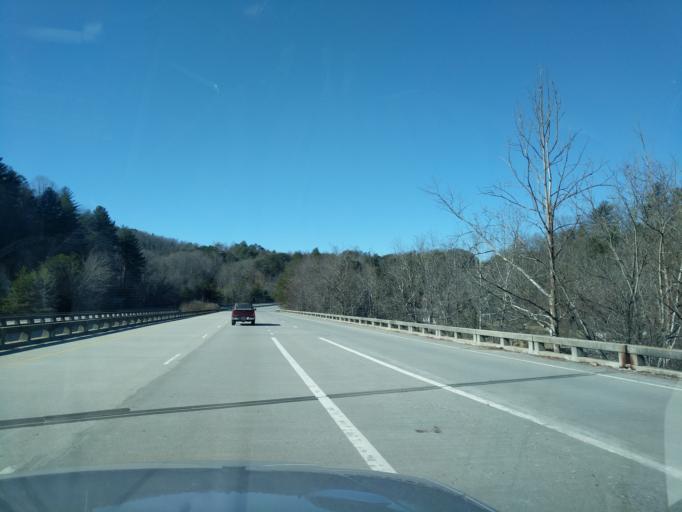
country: US
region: North Carolina
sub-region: Swain County
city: Cherokee
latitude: 35.4309
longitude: -83.3592
